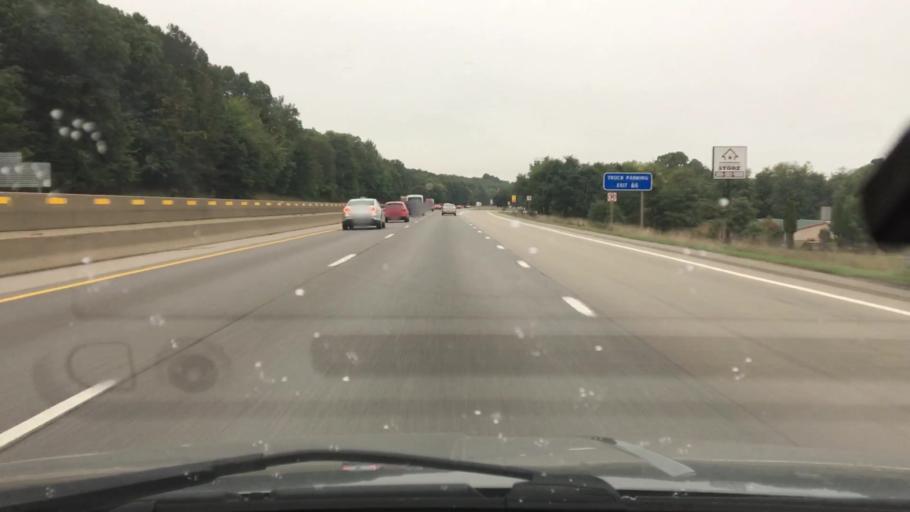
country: US
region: Michigan
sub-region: Kalamazoo County
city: Galesburg
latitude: 42.2724
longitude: -85.4349
